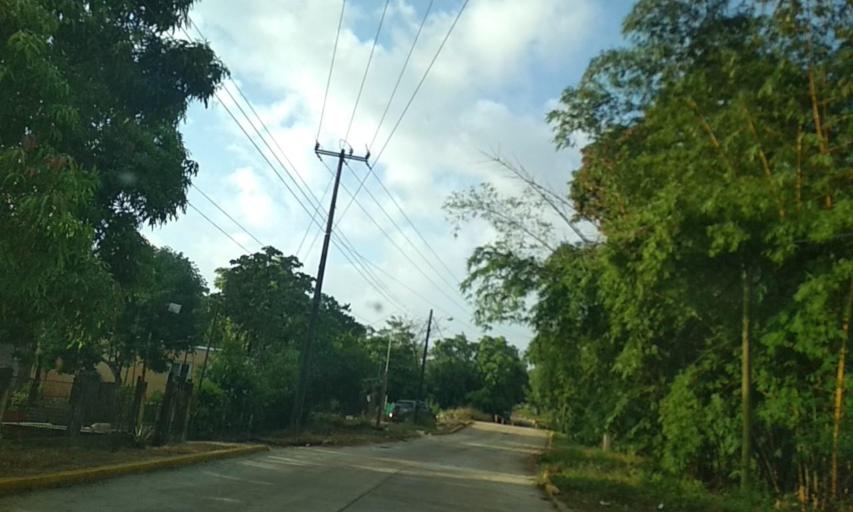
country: MX
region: Veracruz
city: Las Choapas
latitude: 17.8957
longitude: -94.1080
